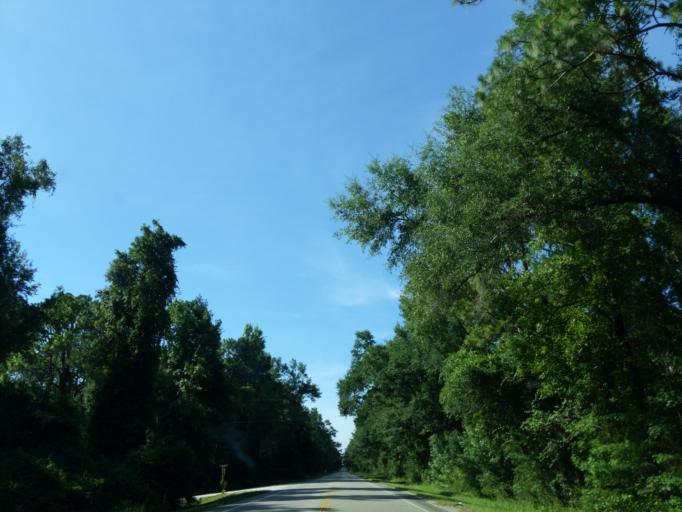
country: US
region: Florida
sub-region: Leon County
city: Woodville
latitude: 30.2946
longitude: -84.3121
